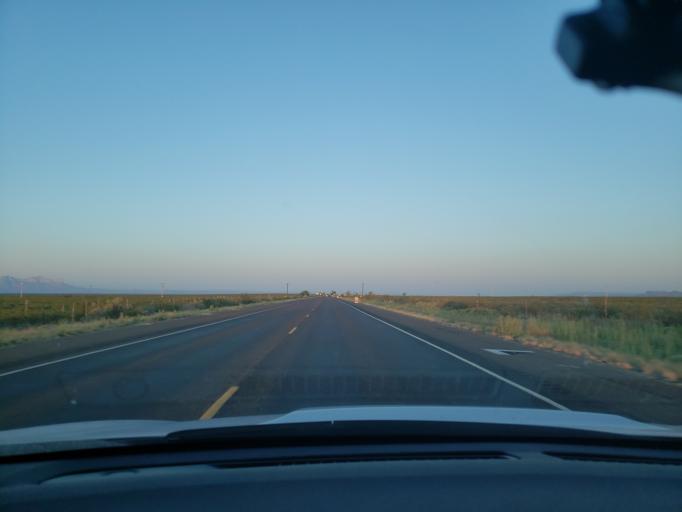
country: US
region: Texas
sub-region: Hudspeth County
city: Sierra Blanca
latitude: 31.7630
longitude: -105.3771
